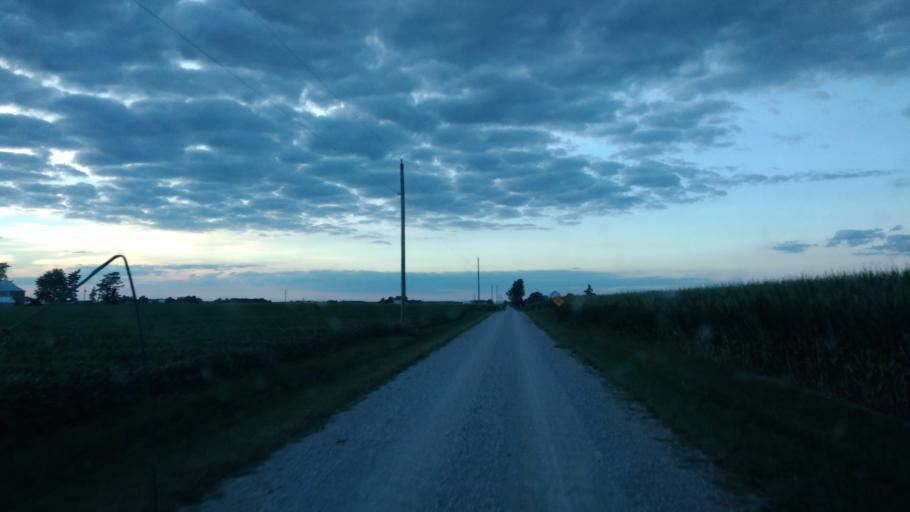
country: US
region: Indiana
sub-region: Adams County
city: Berne
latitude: 40.6384
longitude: -85.0797
